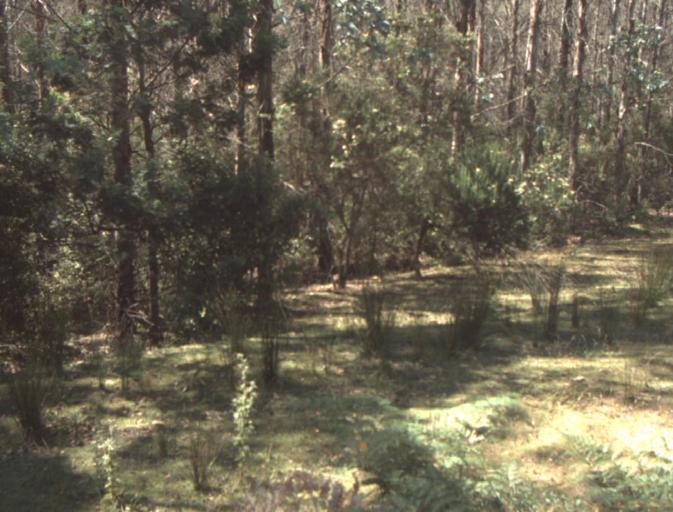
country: AU
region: Tasmania
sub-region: Dorset
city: Scottsdale
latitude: -41.2555
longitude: 147.3458
